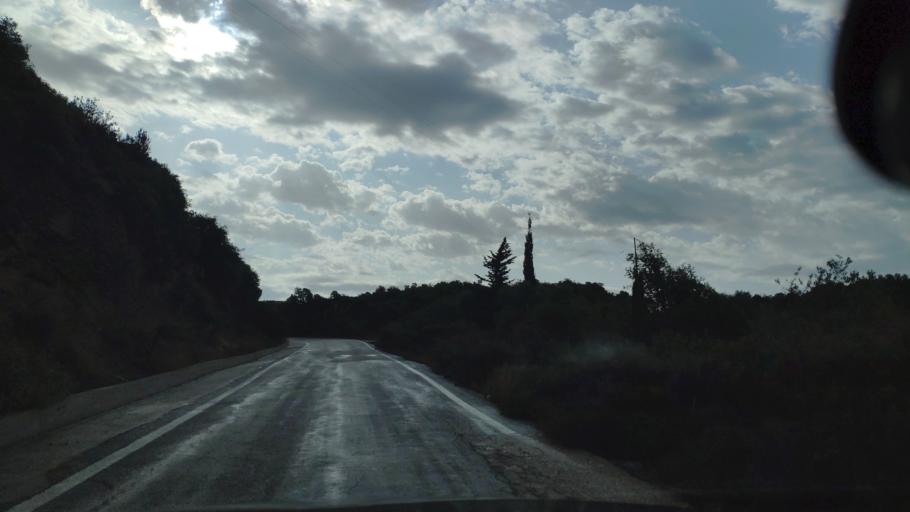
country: GR
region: West Greece
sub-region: Nomos Aitolias kai Akarnanias
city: Sardinia
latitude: 38.8880
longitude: 21.2342
